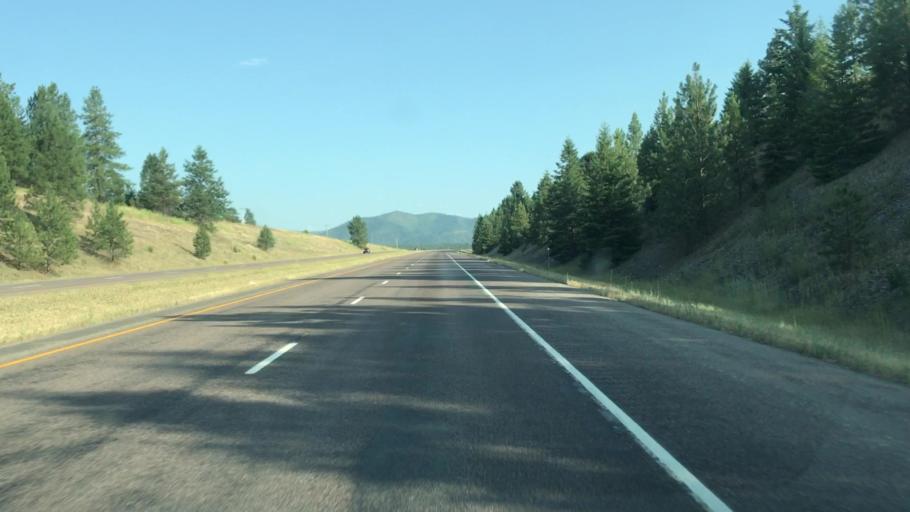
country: US
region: Montana
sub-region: Mineral County
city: Superior
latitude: 47.0510
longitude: -114.7568
